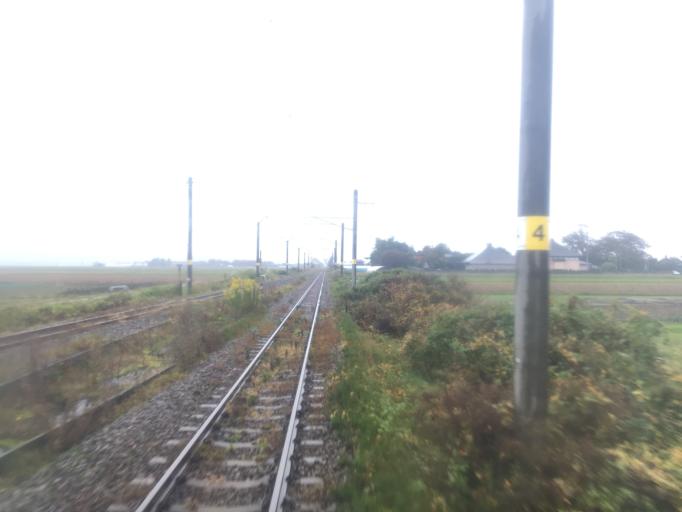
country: JP
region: Yamagata
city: Sakata
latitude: 38.9067
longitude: 139.8787
